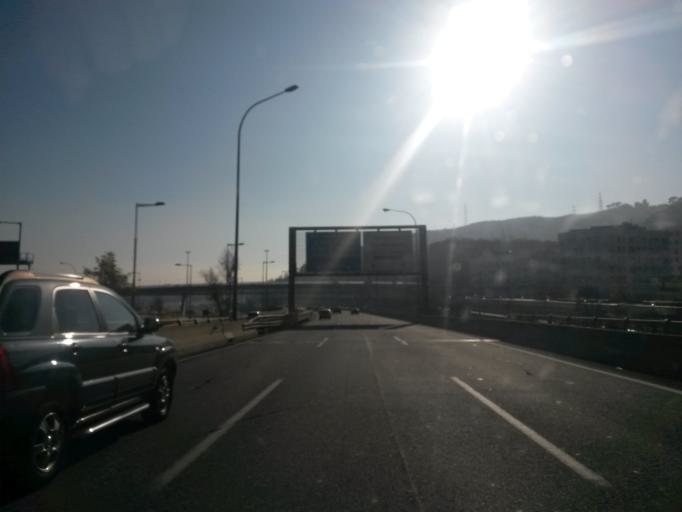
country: ES
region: Catalonia
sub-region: Provincia de Barcelona
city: Nou Barris
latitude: 41.4622
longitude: 2.1806
